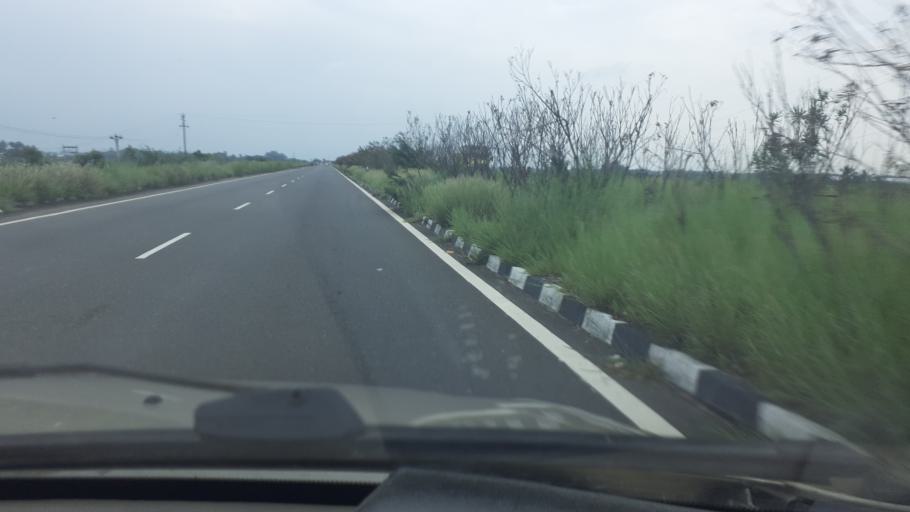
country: IN
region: Tamil Nadu
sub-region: Madurai
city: Tirupparangunram
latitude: 9.8204
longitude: 77.9778
